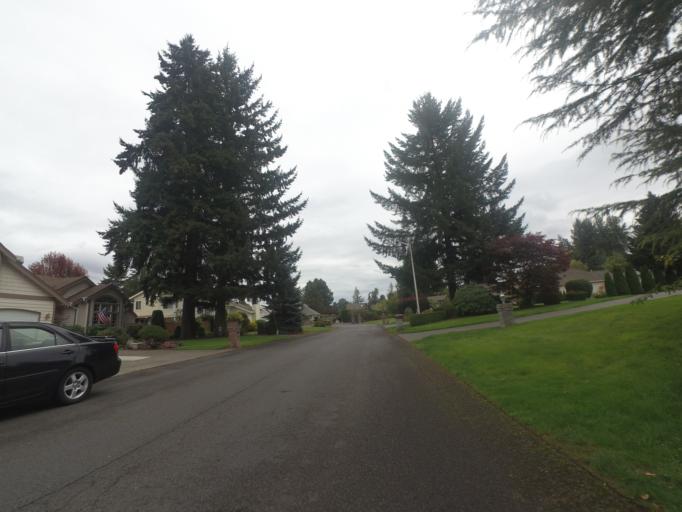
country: US
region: Washington
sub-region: Pierce County
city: Lakewood
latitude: 47.1485
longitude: -122.5115
